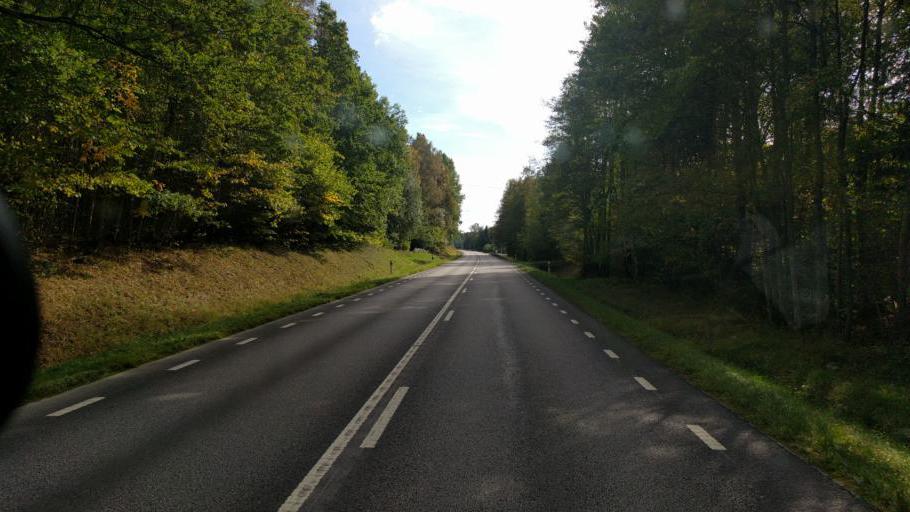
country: SE
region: OEstergoetland
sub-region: Kinda Kommun
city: Kisa
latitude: 57.9370
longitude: 15.6682
